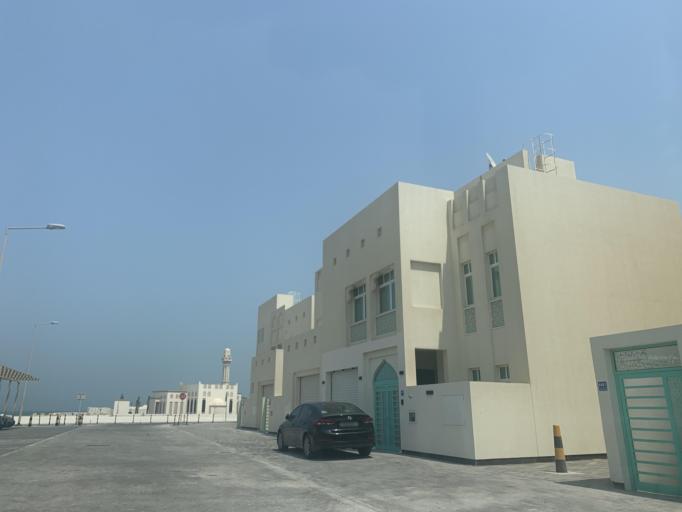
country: BH
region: Muharraq
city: Al Hadd
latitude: 26.2442
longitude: 50.6652
